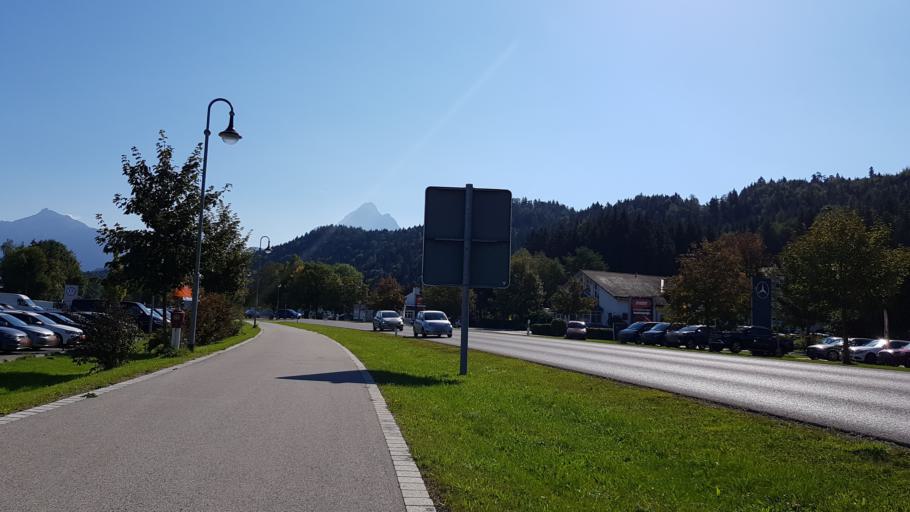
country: DE
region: Bavaria
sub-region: Swabia
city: Fuessen
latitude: 47.5695
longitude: 10.6672
